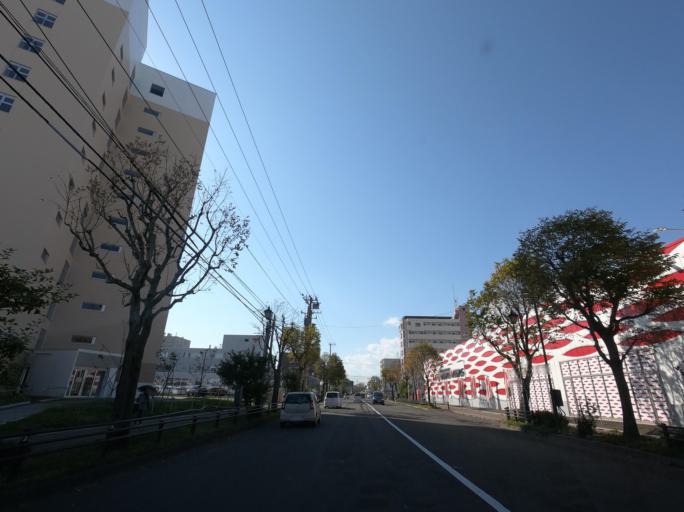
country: JP
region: Hokkaido
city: Kushiro
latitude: 42.9895
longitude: 144.3791
